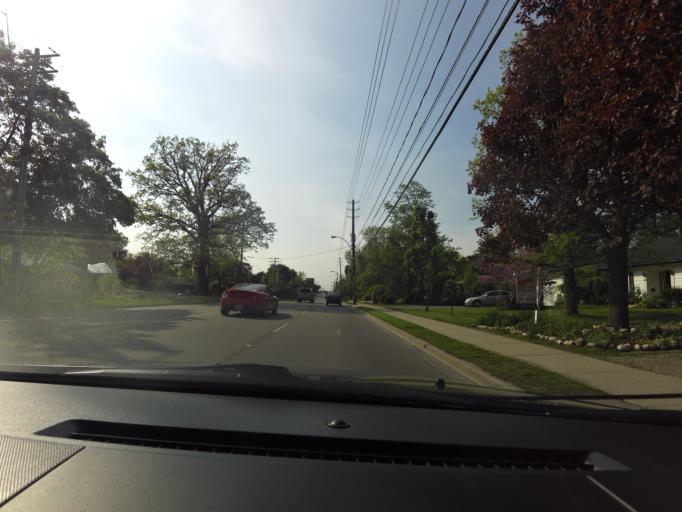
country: CA
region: Ontario
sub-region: Wellington County
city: Guelph
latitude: 43.5265
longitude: -80.2430
